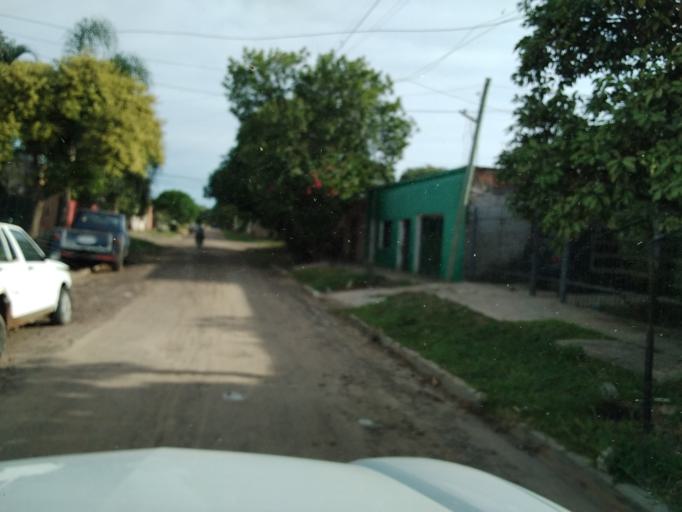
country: AR
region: Corrientes
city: Corrientes
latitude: -27.4905
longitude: -58.8422
